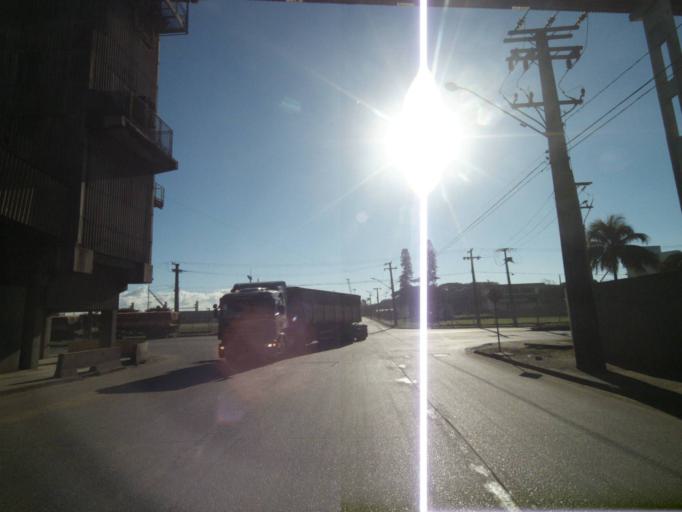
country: BR
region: Parana
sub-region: Paranagua
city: Paranagua
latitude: -25.5067
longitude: -48.5163
